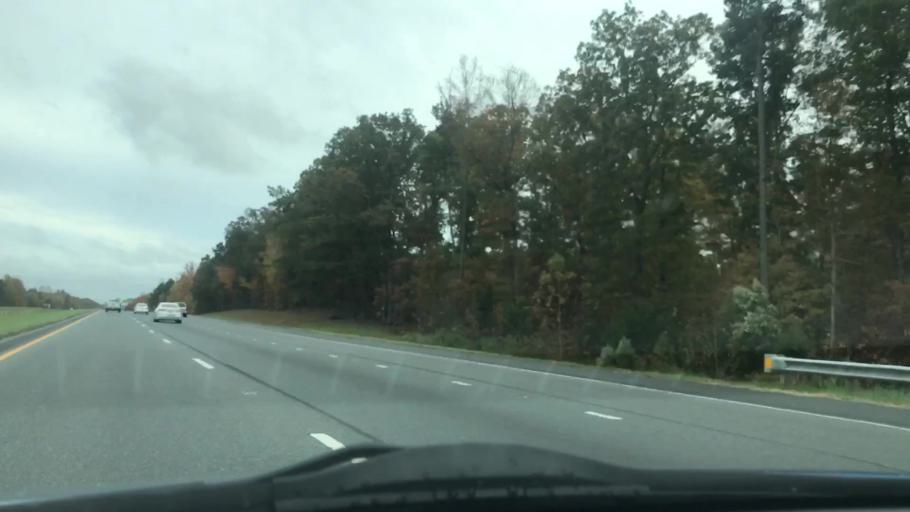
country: US
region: North Carolina
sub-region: Randolph County
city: Randleman
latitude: 35.7809
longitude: -79.8297
